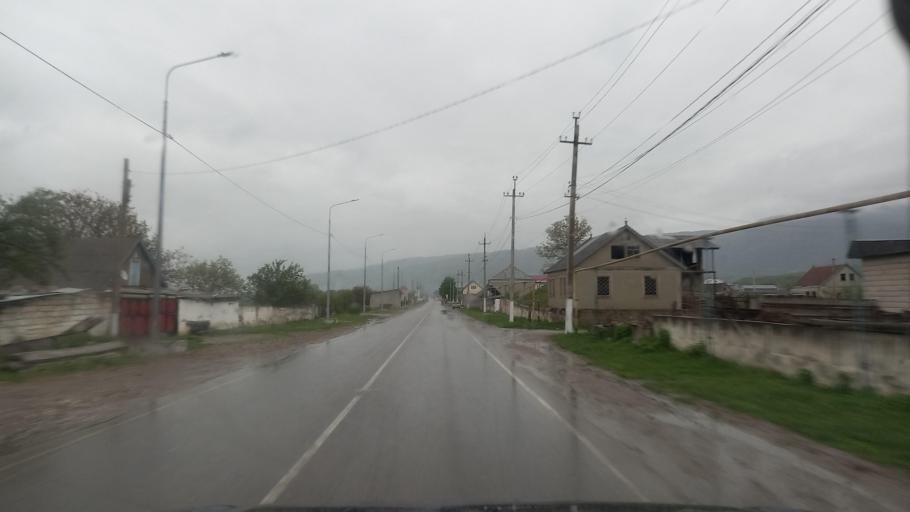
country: RU
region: Kabardino-Balkariya
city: Zhankhoteko
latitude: 43.5895
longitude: 43.1999
